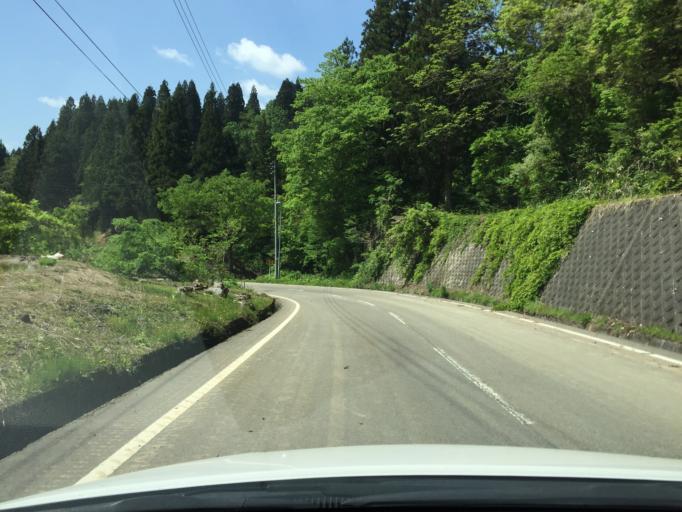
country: JP
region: Niigata
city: Tochio-honcho
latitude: 37.4922
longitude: 139.0543
